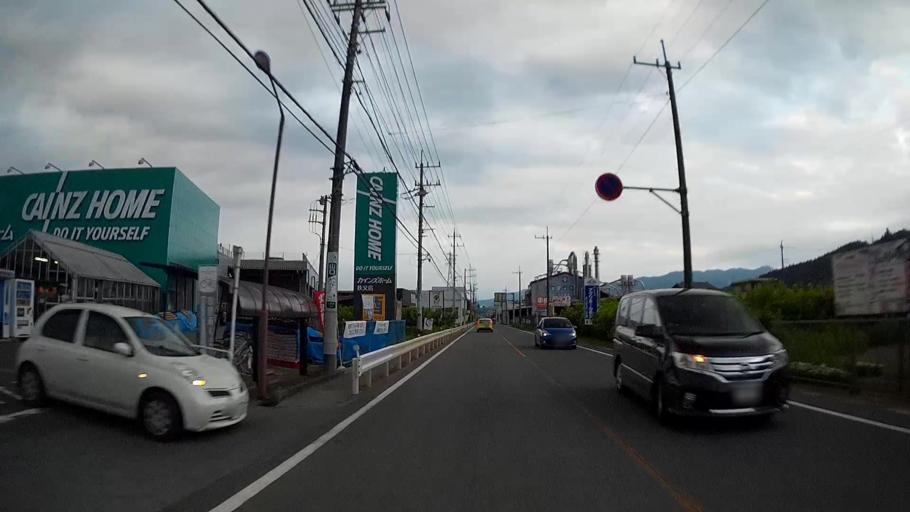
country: JP
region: Saitama
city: Chichibu
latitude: 35.9713
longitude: 139.0644
